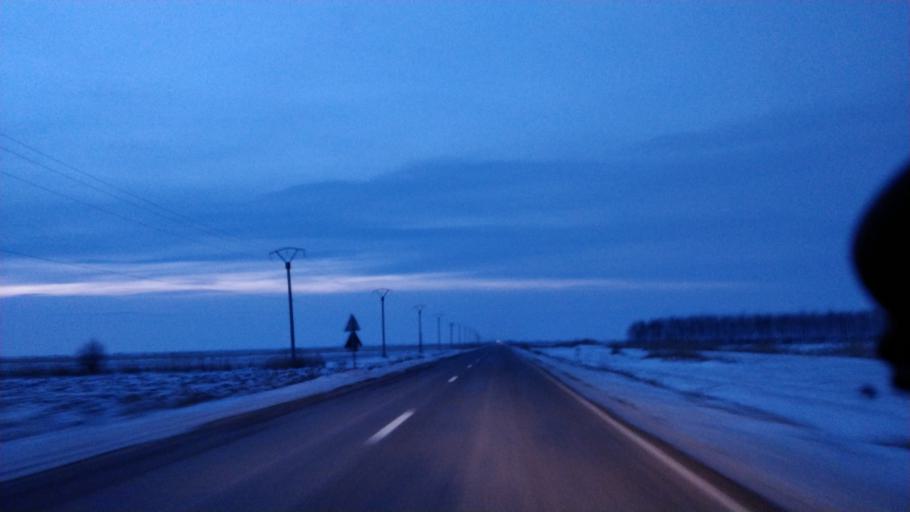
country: RO
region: Vrancea
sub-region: Comuna Vulturu
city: Vadu Rosca
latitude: 45.5964
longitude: 27.4669
